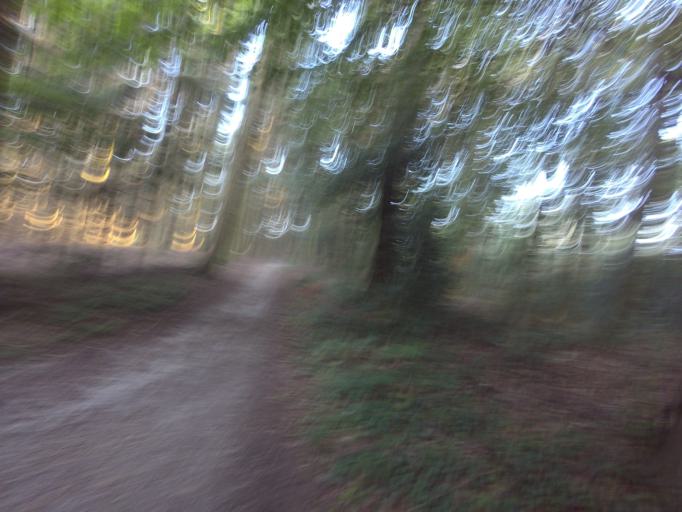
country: BE
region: Wallonia
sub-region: Province de Liege
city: Plombieres
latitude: 50.7611
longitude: 5.9665
